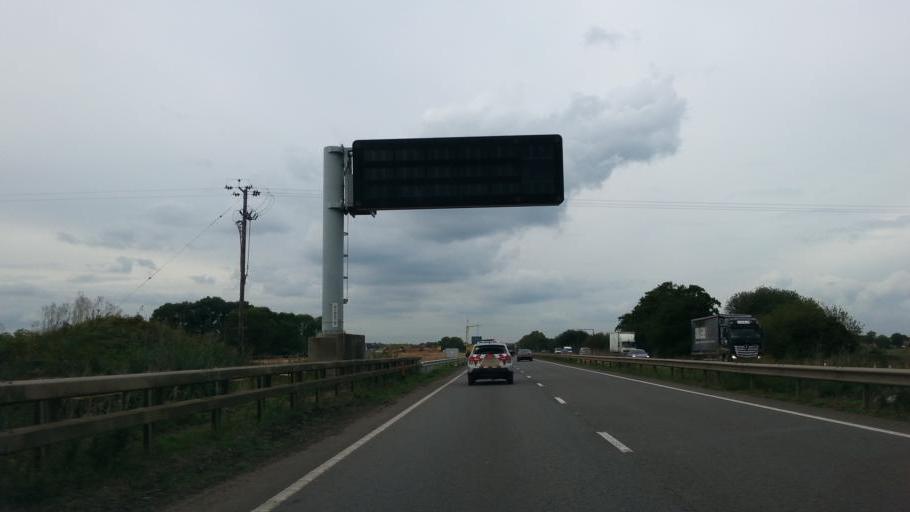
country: GB
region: England
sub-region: Cambridgeshire
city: Buckden
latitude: 52.3168
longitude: -0.2445
